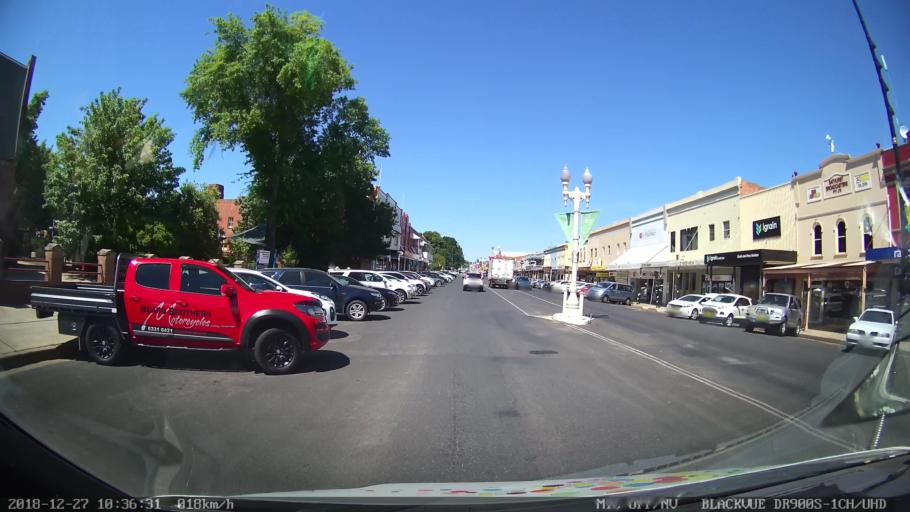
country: AU
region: New South Wales
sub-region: Bathurst Regional
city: Bathurst
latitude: -33.4160
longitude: 149.5797
